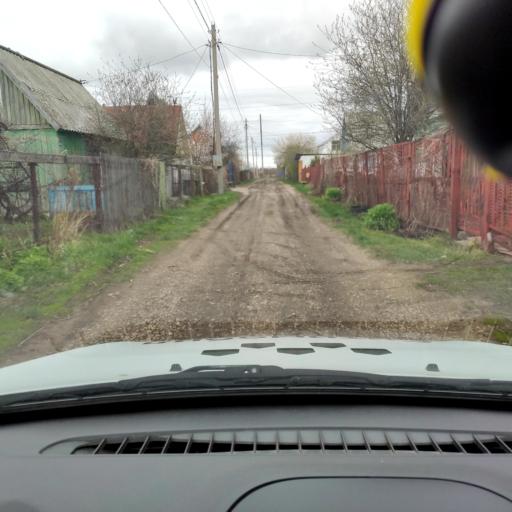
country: RU
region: Samara
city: Tol'yatti
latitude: 53.5857
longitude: 49.3165
